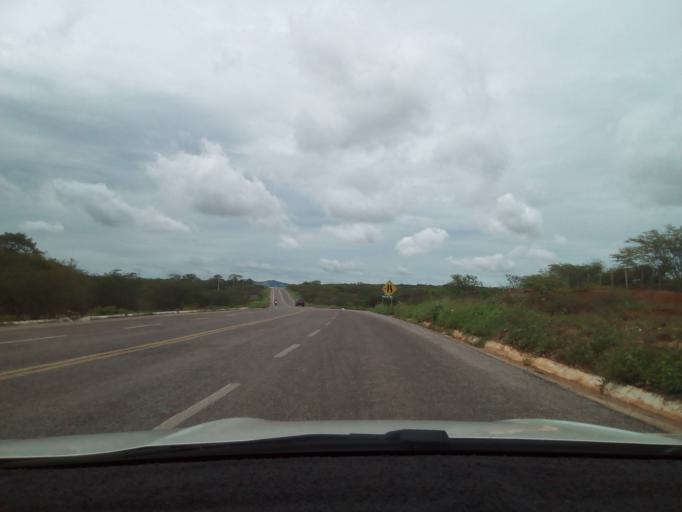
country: BR
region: Rio Grande do Norte
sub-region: Patu
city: Patu
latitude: -6.1487
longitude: -37.7539
